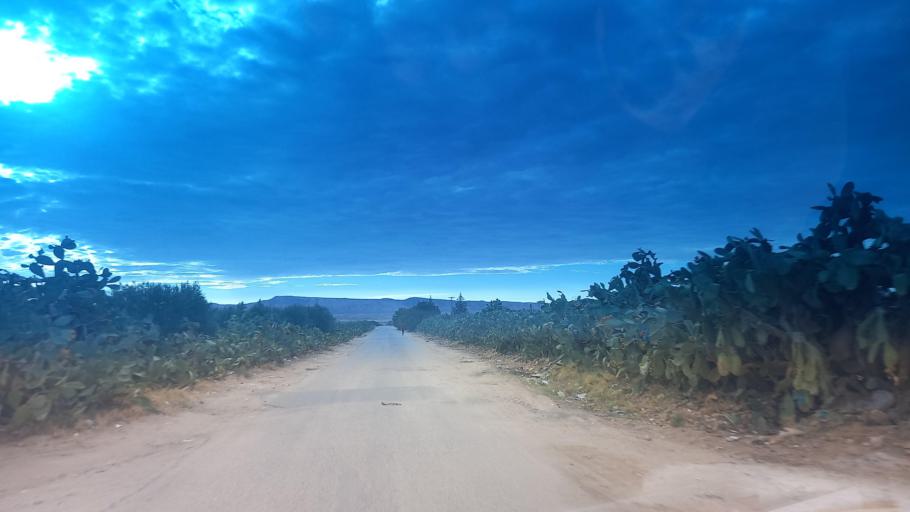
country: TN
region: Al Qasrayn
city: Sbiba
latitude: 35.3809
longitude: 9.0538
